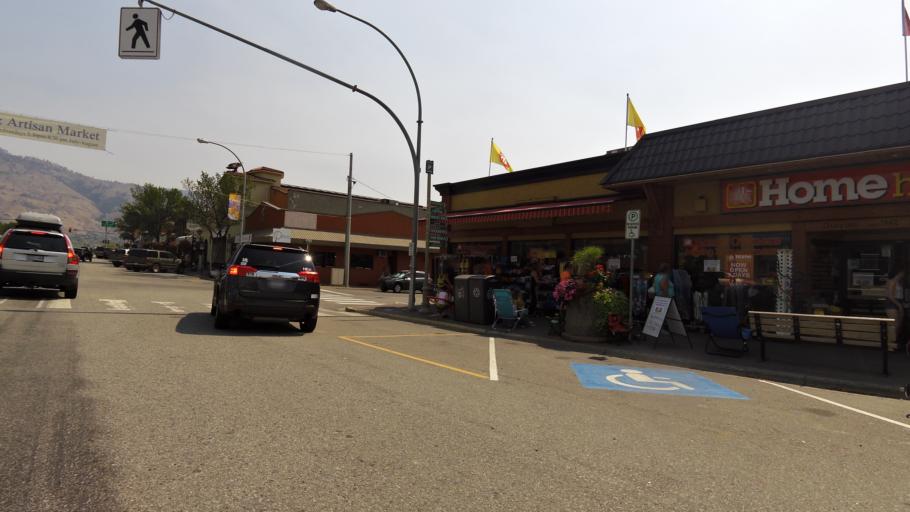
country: CA
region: British Columbia
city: Osoyoos
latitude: 49.0328
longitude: -119.4656
